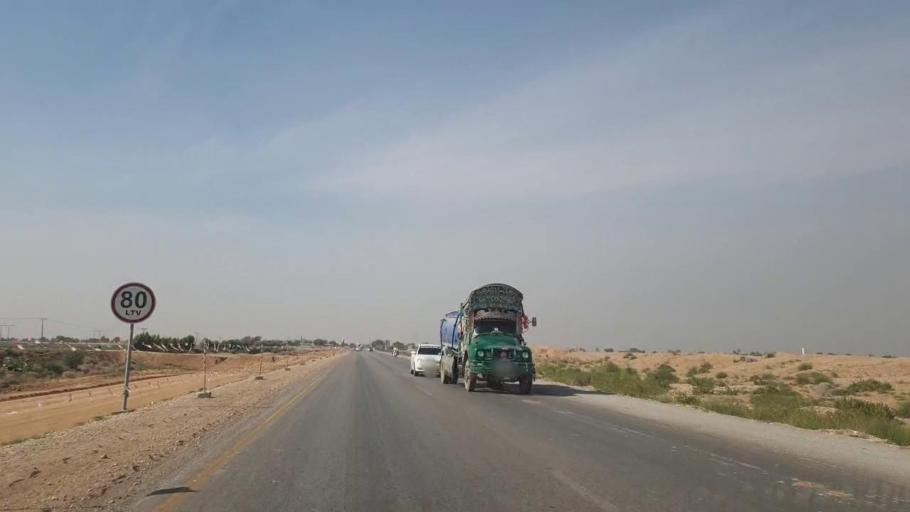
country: PK
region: Sindh
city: Sann
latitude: 26.0241
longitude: 68.1306
